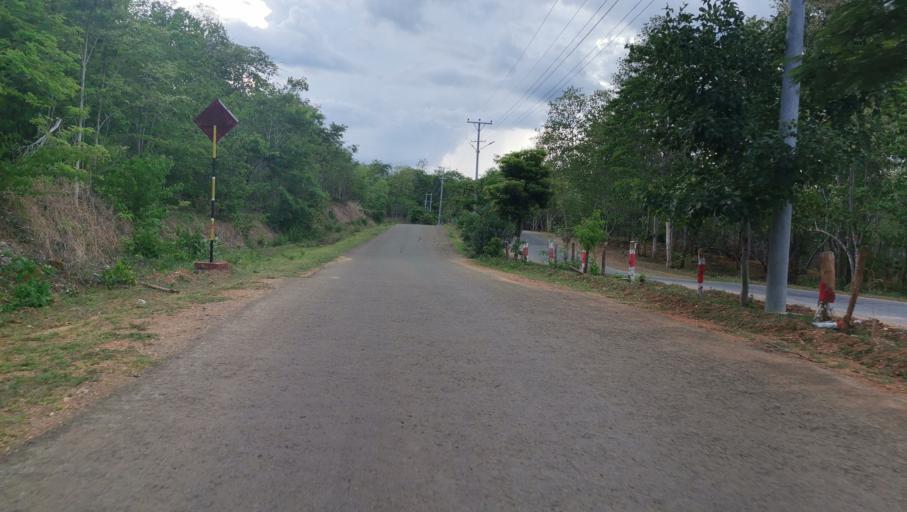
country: MM
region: Magway
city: Minbu
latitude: 20.0869
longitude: 94.5733
